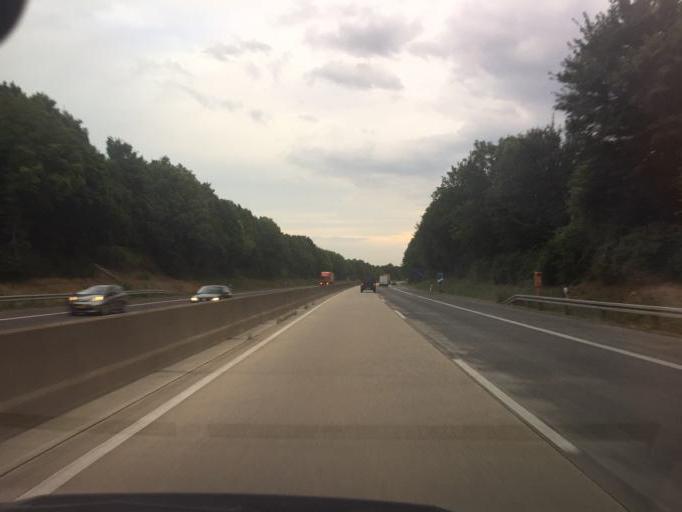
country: DE
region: North Rhine-Westphalia
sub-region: Regierungsbezirk Koln
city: Bedburg
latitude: 50.9981
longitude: 6.5412
